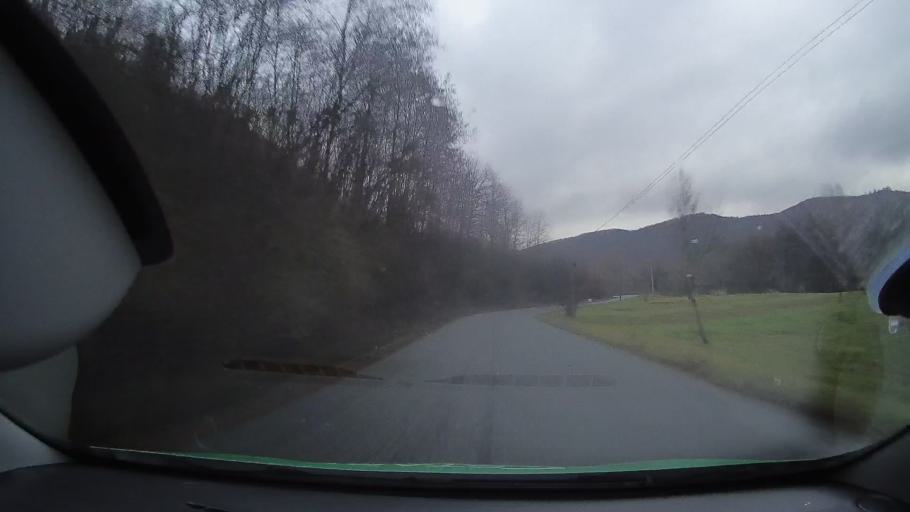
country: RO
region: Hunedoara
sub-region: Comuna Baia de Cris
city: Baia de Cris
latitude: 46.2030
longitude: 22.7181
